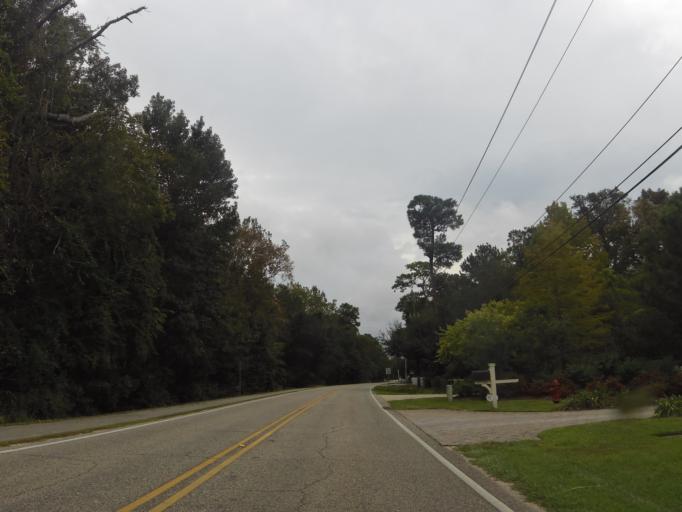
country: US
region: Alabama
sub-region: Baldwin County
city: Point Clear
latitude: 30.4829
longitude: -87.9302
